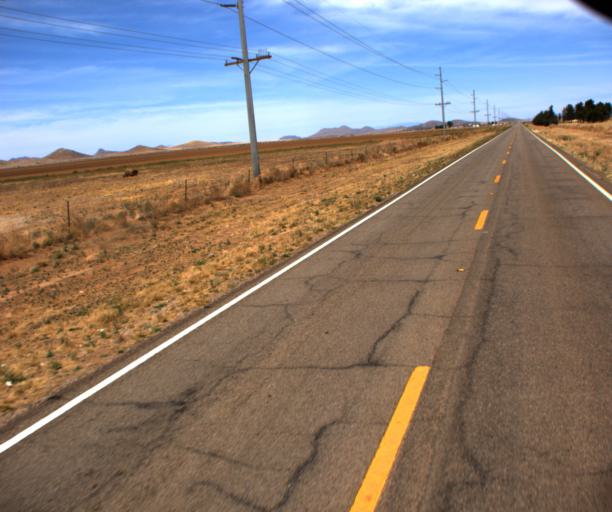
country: US
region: Arizona
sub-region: Cochise County
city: Tombstone
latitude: 31.8260
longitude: -109.6952
